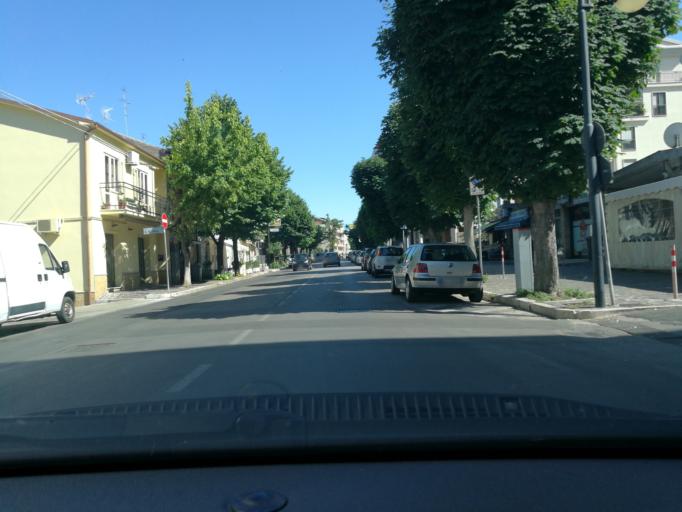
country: IT
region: Abruzzo
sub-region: Provincia di Chieti
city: Vasto
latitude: 42.1207
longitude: 14.7066
